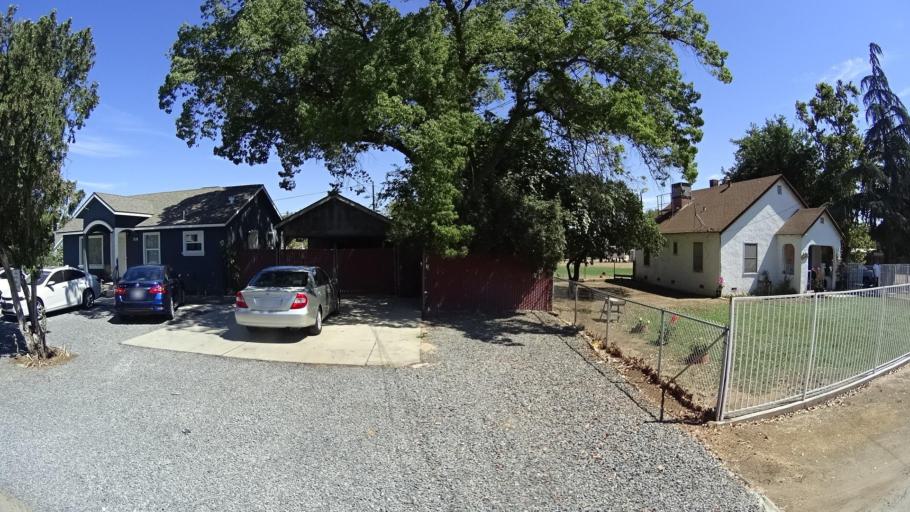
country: US
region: California
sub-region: Fresno County
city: Sunnyside
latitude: 36.7459
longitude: -119.7247
